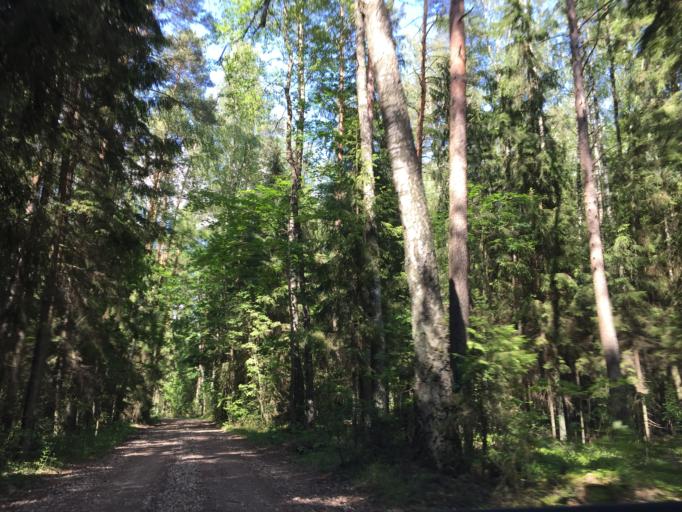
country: LV
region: Engure
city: Smarde
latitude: 56.8196
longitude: 23.3904
